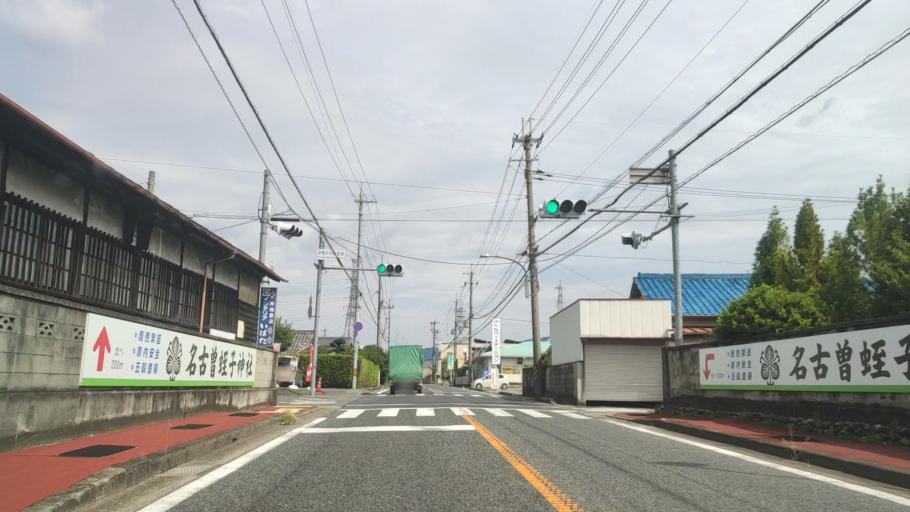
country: JP
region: Wakayama
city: Hashimoto
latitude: 34.3031
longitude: 135.5628
